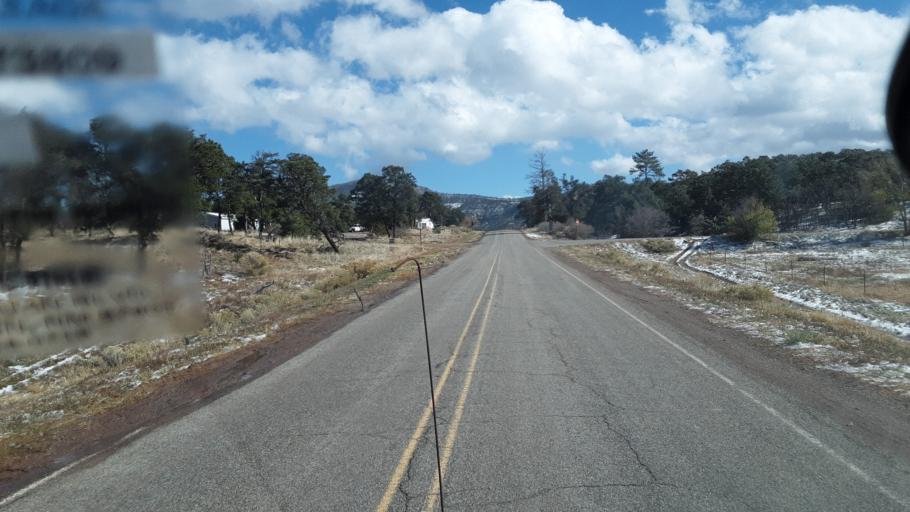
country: US
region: New Mexico
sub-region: Rio Arriba County
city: Santa Teresa
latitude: 36.2285
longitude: -106.8204
